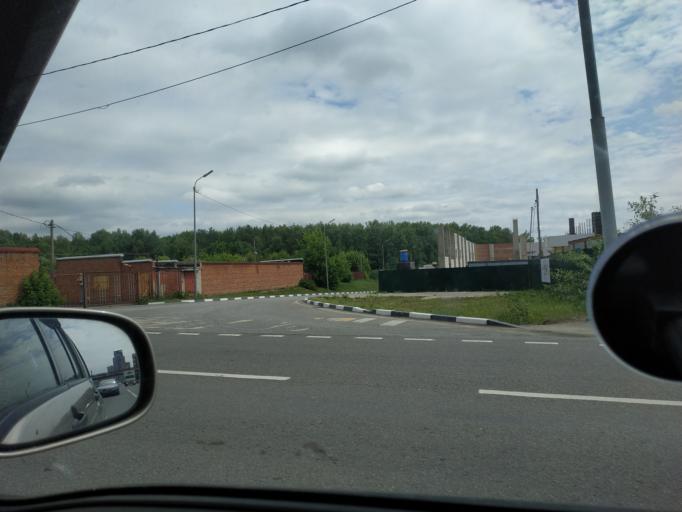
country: RU
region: Moskovskaya
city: Shchelkovo
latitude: 55.9297
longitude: 38.0104
